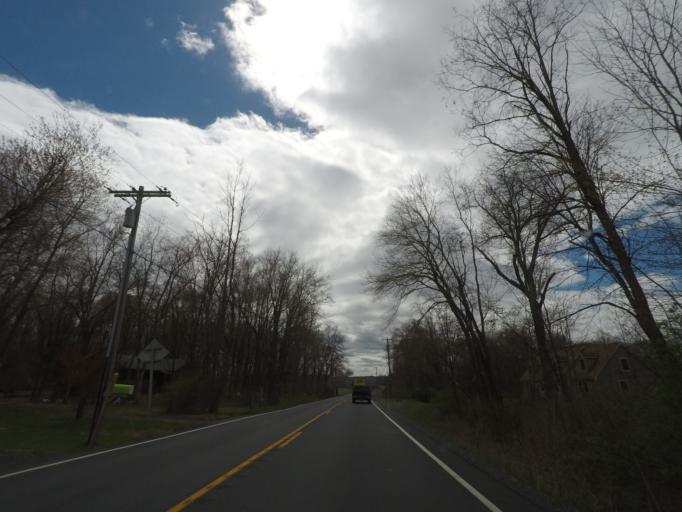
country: US
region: New York
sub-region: Rensselaer County
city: Castleton-on-Hudson
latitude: 42.5059
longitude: -73.7885
